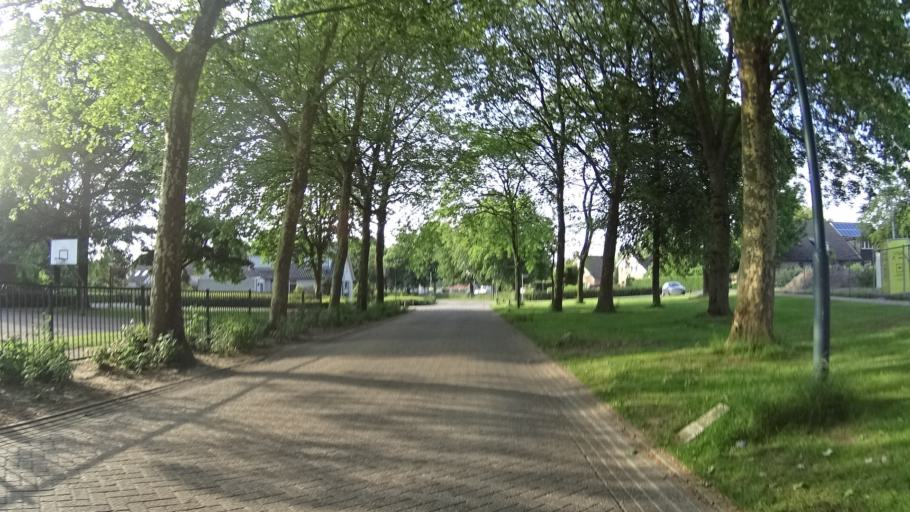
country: NL
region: North Brabant
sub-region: Gemeente Heusden
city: Heusden
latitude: 51.7257
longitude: 5.1388
